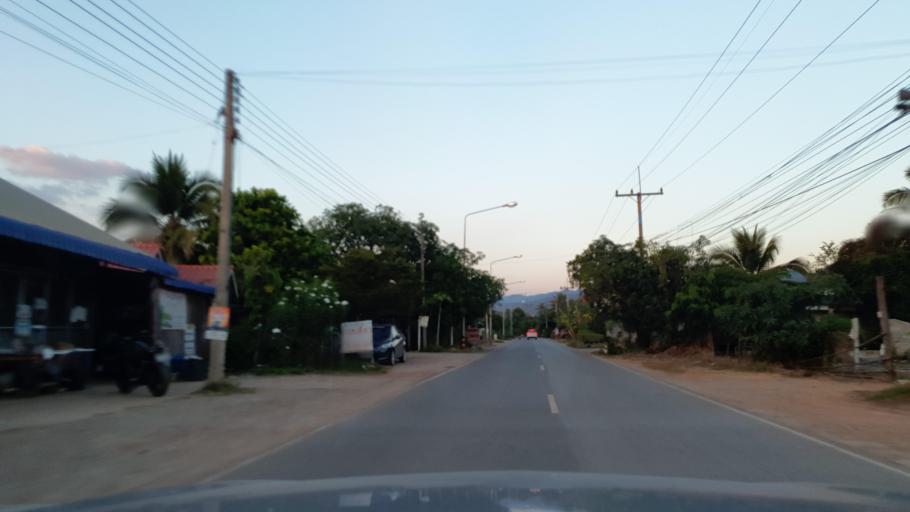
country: TH
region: Phayao
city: Dok Kham Tai
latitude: 19.0316
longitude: 100.0647
